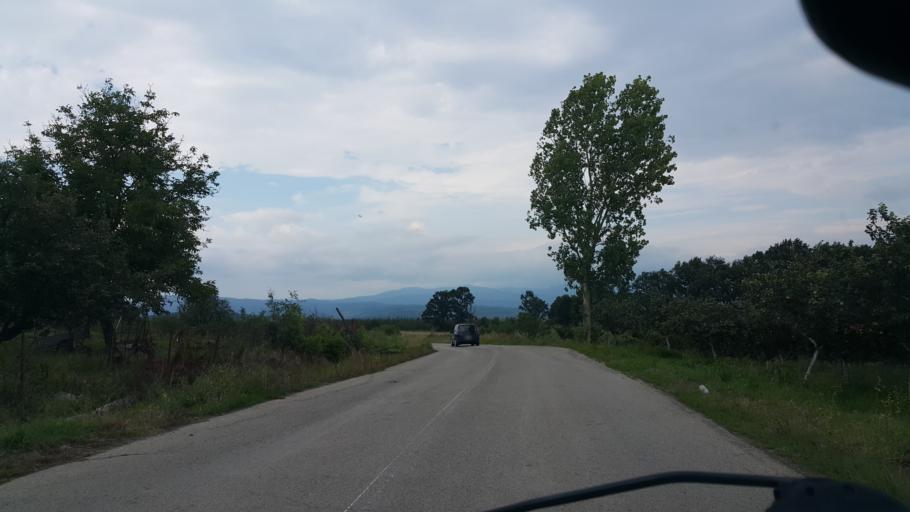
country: RS
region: Central Serbia
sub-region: Toplicki Okrug
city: Blace
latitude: 43.2634
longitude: 21.2723
